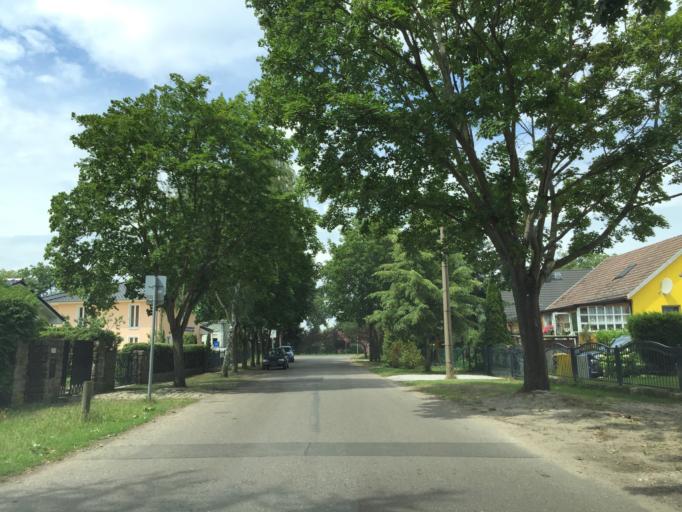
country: DE
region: Berlin
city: Mahlsdorf
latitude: 52.4917
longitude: 13.6095
